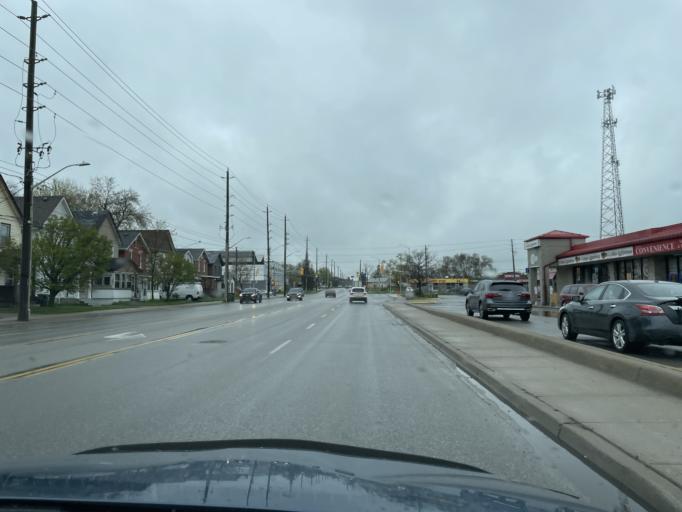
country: CA
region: Ontario
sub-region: Wellington County
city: Guelph
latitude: 43.5511
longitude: -80.2226
